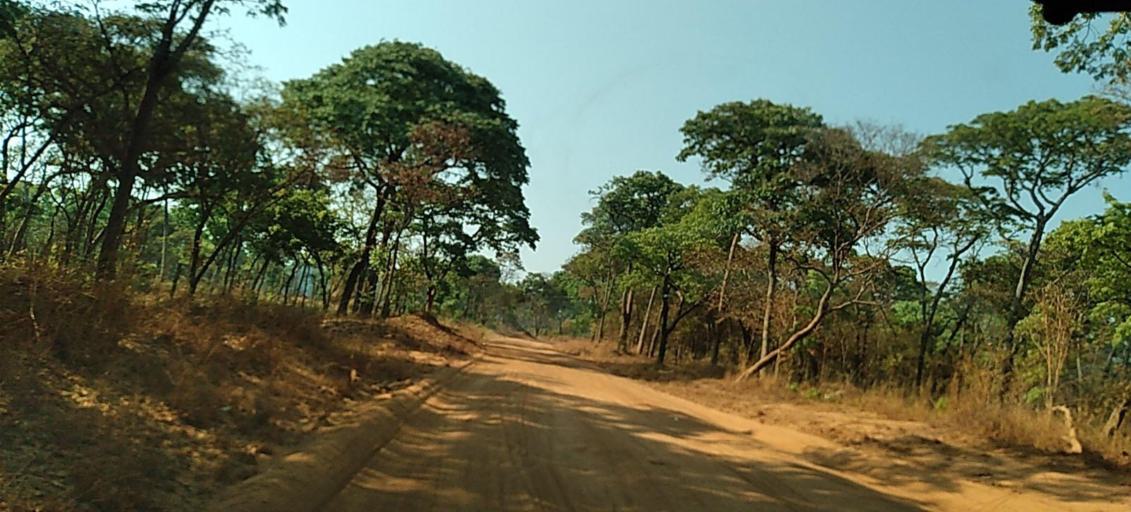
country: ZM
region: North-Western
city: Kasempa
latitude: -13.6569
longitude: 26.0086
